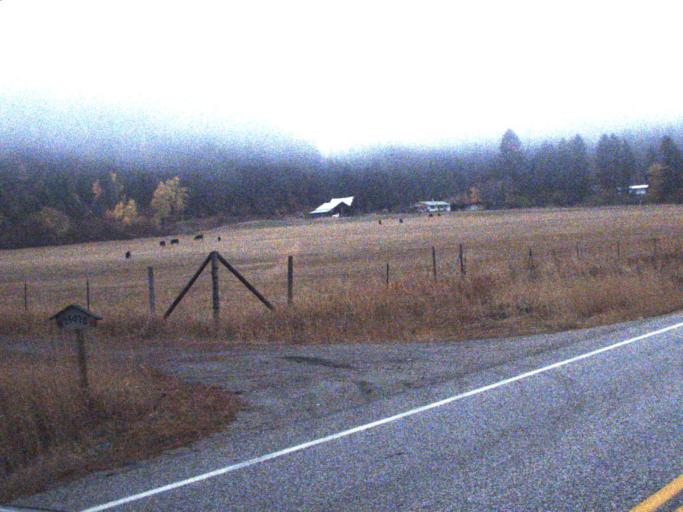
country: US
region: Washington
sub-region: Stevens County
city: Kettle Falls
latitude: 48.7339
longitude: -118.1313
